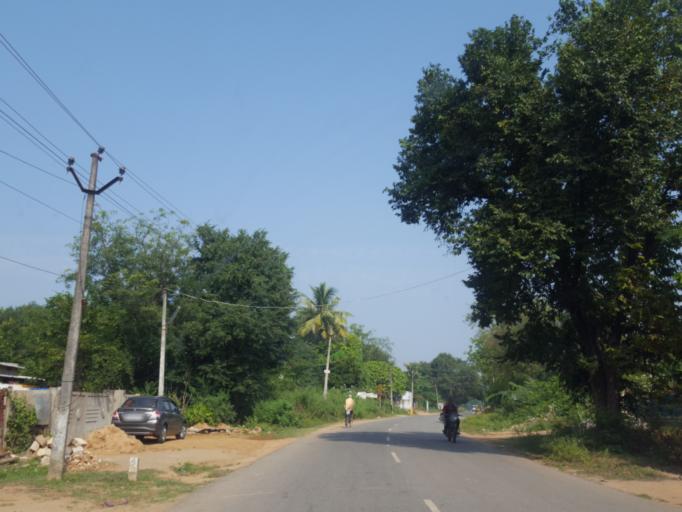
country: IN
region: Telangana
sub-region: Khammam
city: Yellandu
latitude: 17.6124
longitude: 80.3113
